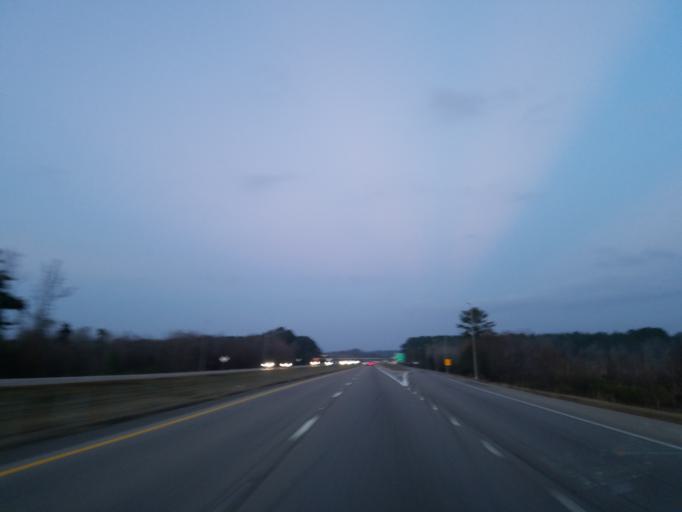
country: US
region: Alabama
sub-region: Sumter County
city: York
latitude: 32.4324
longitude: -88.4459
